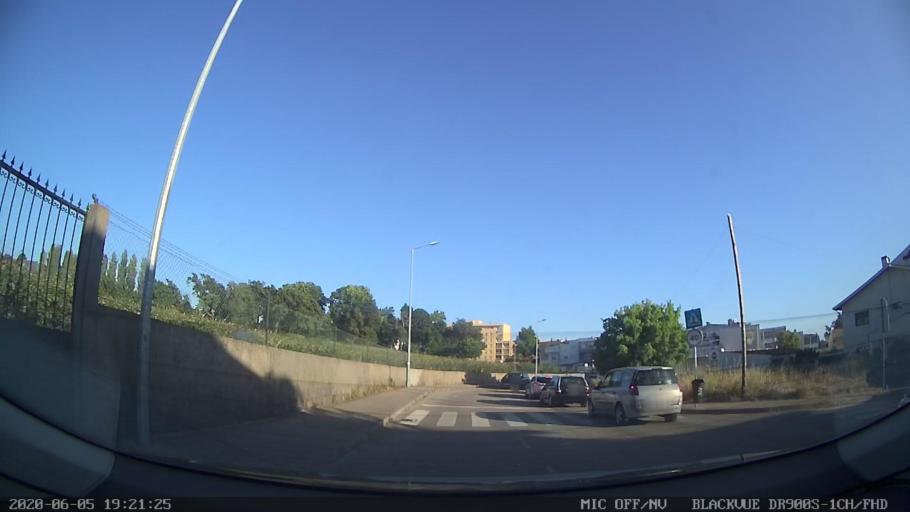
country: PT
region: Porto
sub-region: Gondomar
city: Baguim do Monte
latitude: 41.2075
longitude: -8.5472
